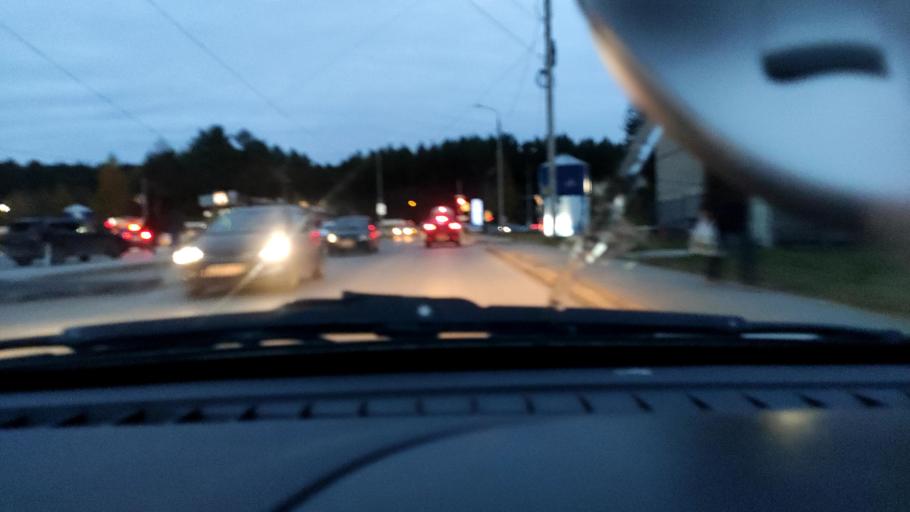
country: RU
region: Perm
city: Kondratovo
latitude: 58.0354
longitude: 56.1442
